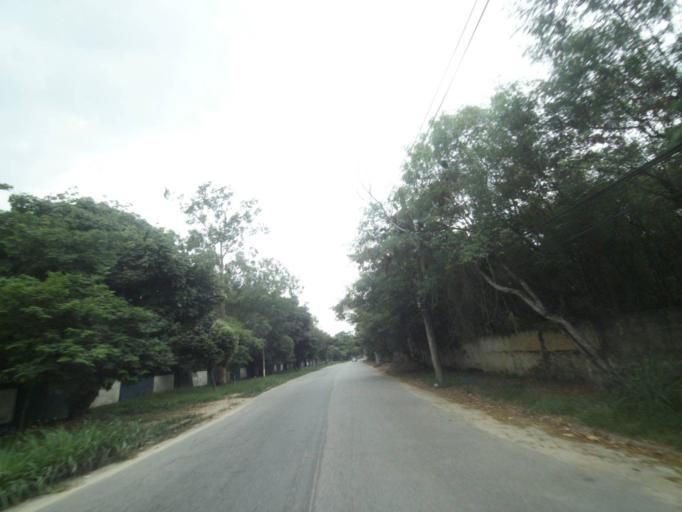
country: BR
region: Rio de Janeiro
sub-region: Nilopolis
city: Nilopolis
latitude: -22.8852
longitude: -43.3935
